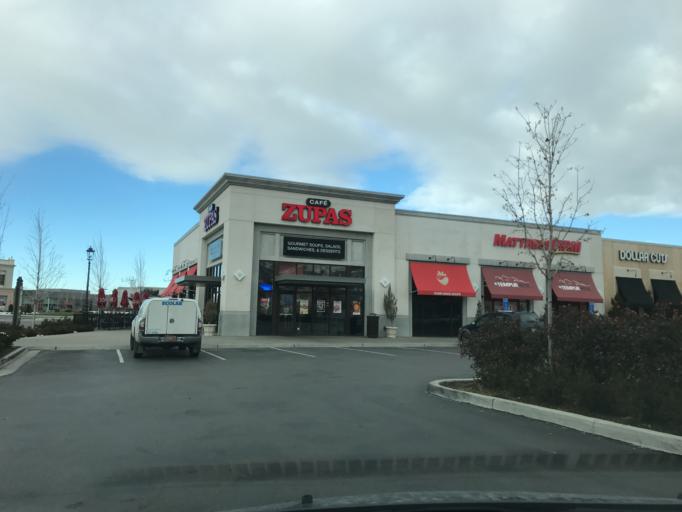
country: US
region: Utah
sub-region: Davis County
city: Farmington
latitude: 40.9851
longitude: -111.9058
